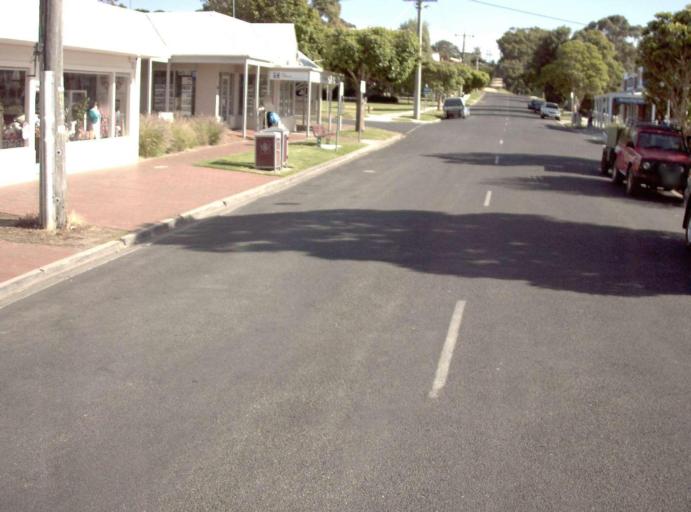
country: AU
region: Victoria
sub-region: East Gippsland
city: Lakes Entrance
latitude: -37.8927
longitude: 147.8535
